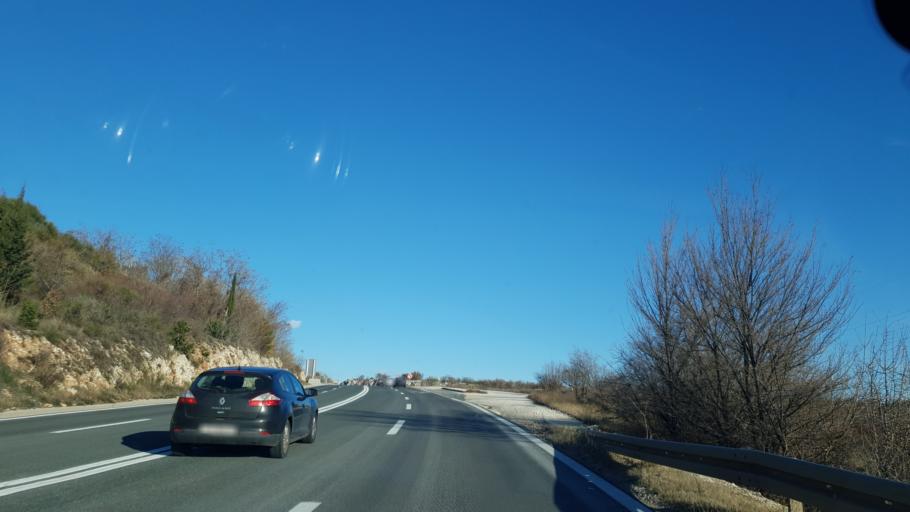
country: HR
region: Splitsko-Dalmatinska
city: Dugopolje
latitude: 43.6068
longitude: 16.5973
